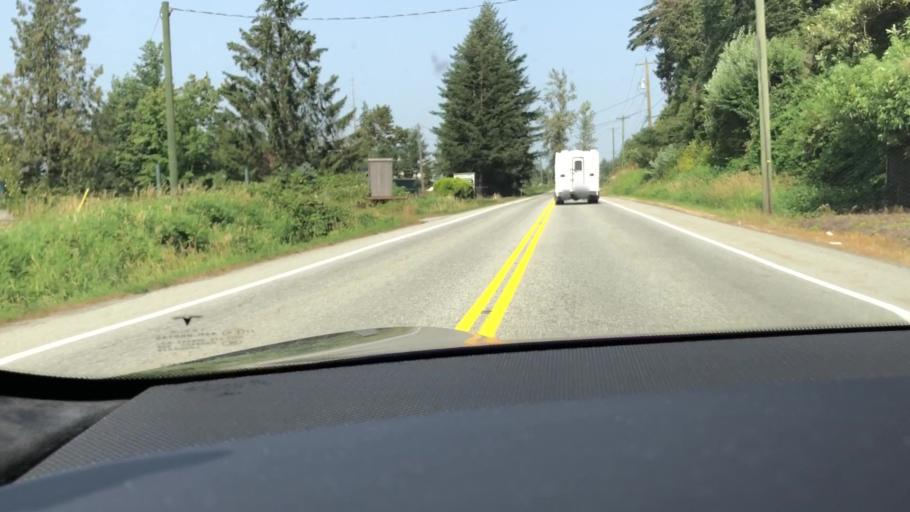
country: CA
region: British Columbia
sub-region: Fraser Valley Regional District
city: Chilliwack
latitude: 49.0847
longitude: -122.0280
